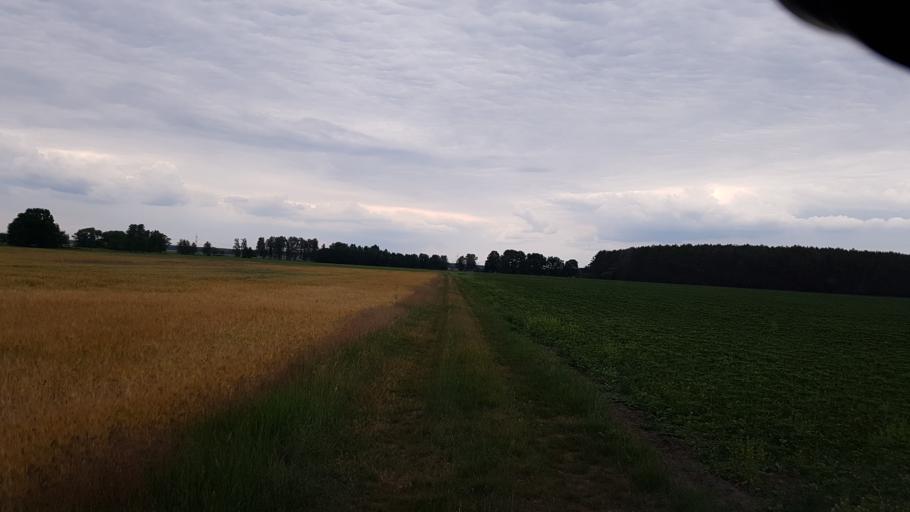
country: DE
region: Brandenburg
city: Ihlow
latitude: 51.8186
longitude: 13.2406
